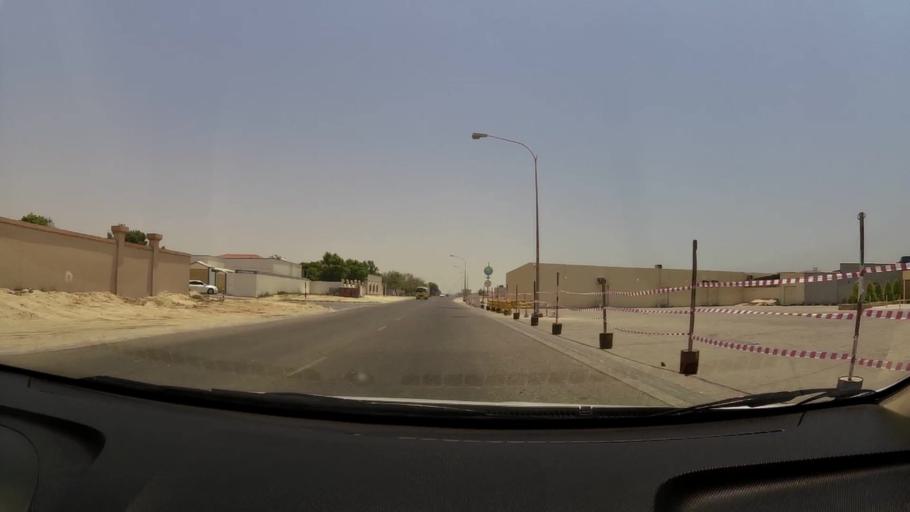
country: AE
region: Umm al Qaywayn
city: Umm al Qaywayn
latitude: 25.5476
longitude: 55.5386
